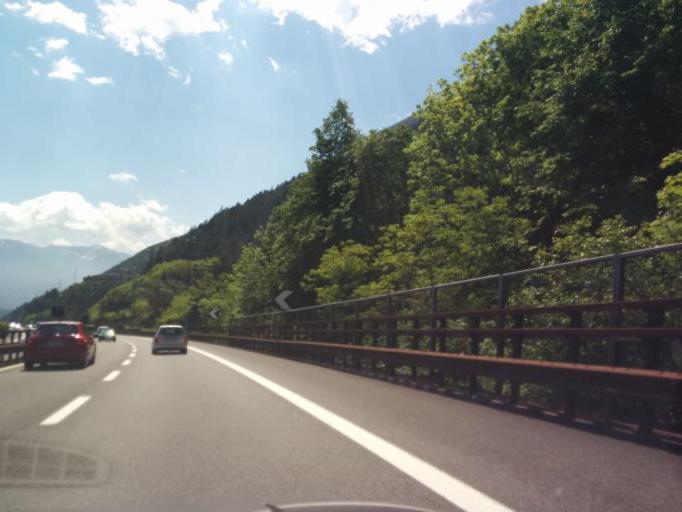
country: IT
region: Trentino-Alto Adige
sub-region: Bolzano
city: Fortezza
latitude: 46.7821
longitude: 11.6175
